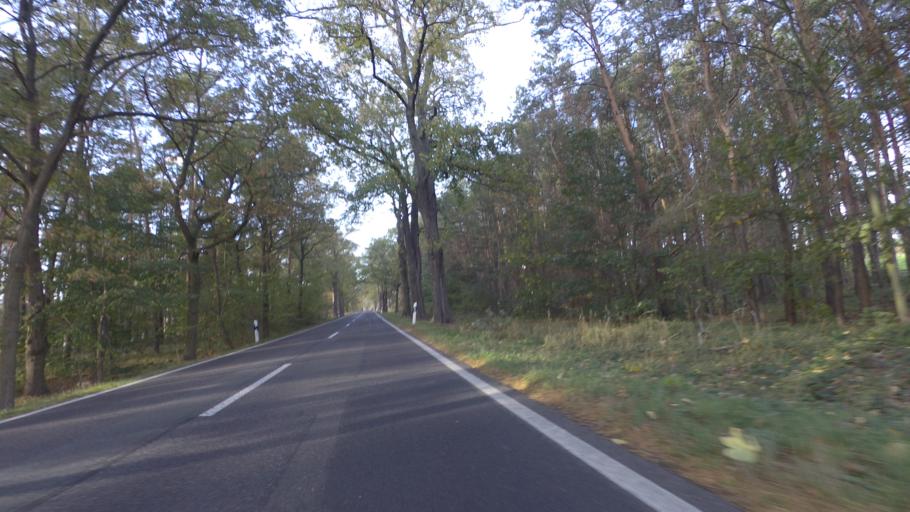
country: DE
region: Brandenburg
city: Sperenberg
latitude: 52.1992
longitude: 13.3119
